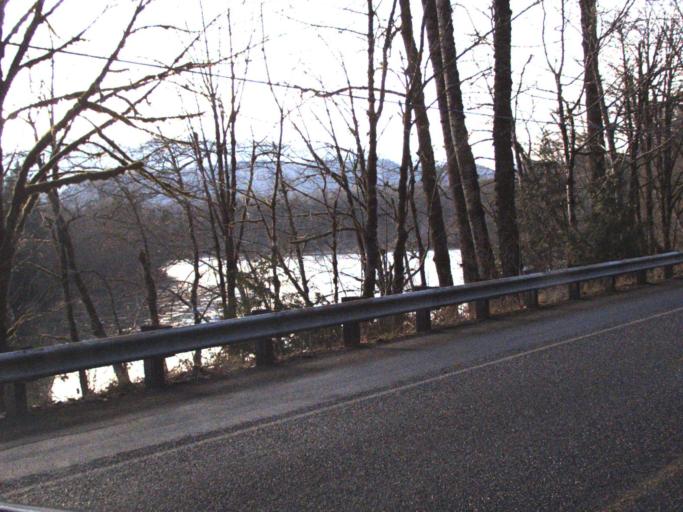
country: US
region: Washington
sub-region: Snohomish County
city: Darrington
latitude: 48.5347
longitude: -121.7323
